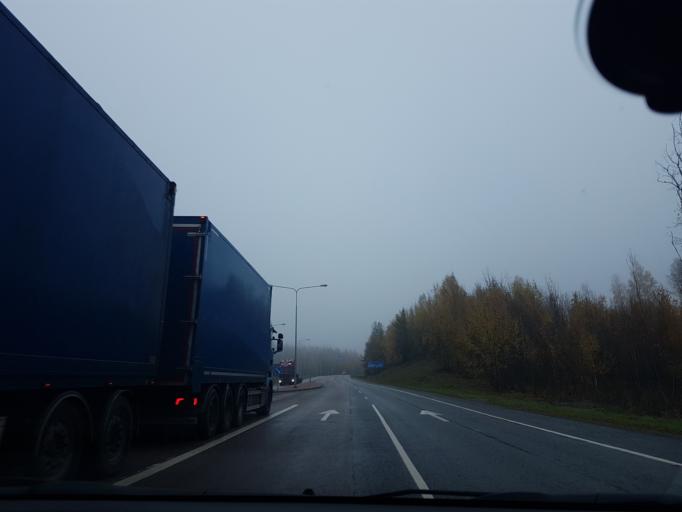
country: FI
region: Uusimaa
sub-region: Helsinki
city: Jaervenpaeae
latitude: 60.4528
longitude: 25.1307
